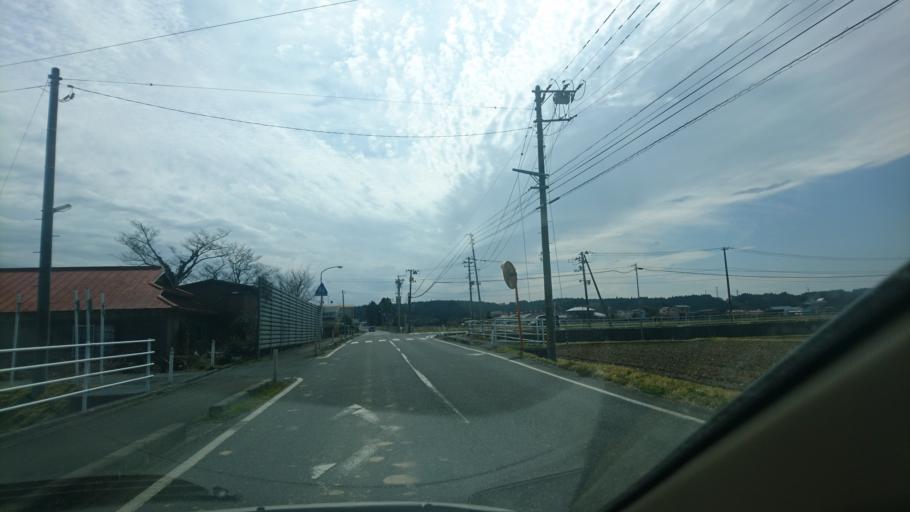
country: JP
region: Miyagi
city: Furukawa
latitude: 38.7439
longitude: 140.9480
